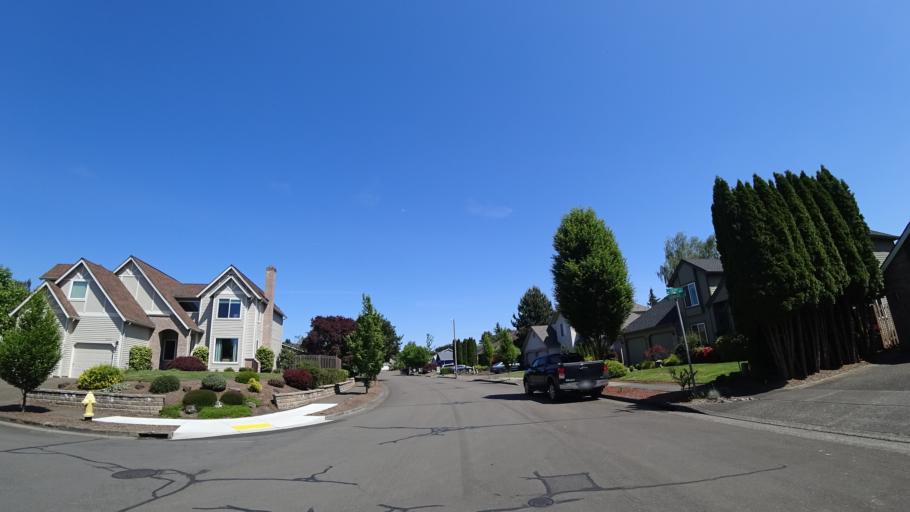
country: US
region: Oregon
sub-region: Washington County
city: King City
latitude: 45.4445
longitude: -122.8139
